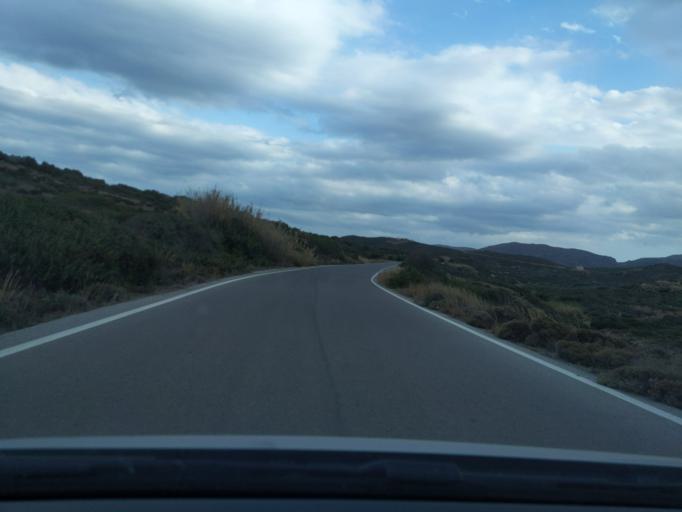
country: GR
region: Crete
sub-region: Nomos Lasithiou
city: Palekastro
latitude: 35.2306
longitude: 26.2535
